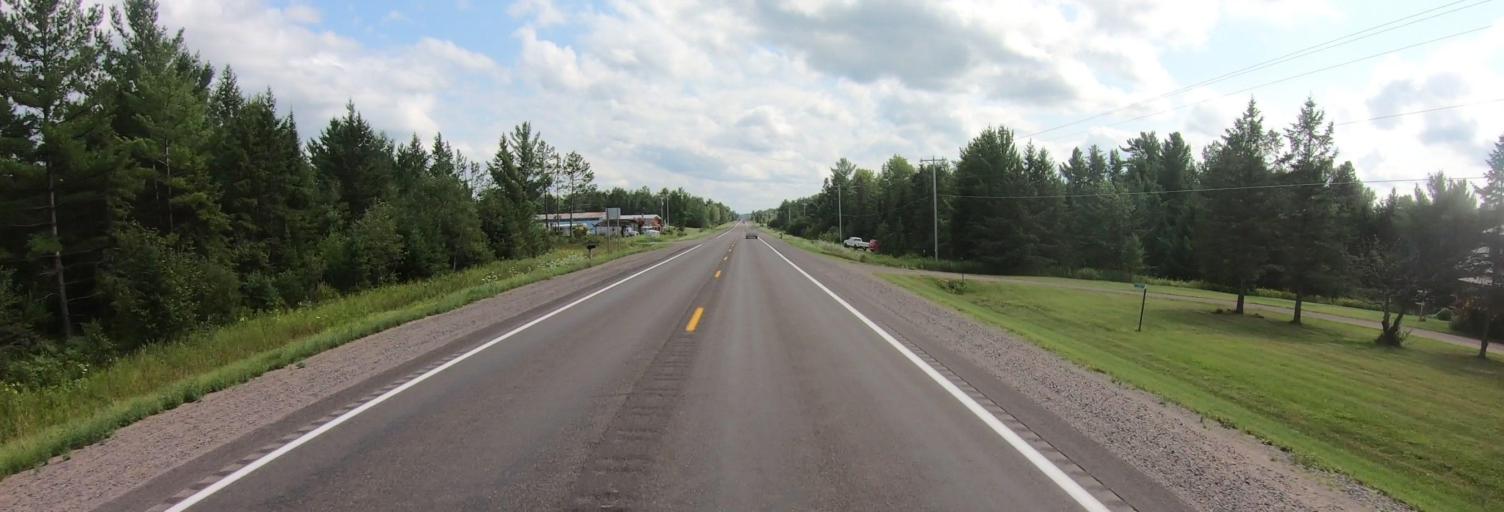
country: US
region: Michigan
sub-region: Ontonagon County
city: Ontonagon
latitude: 46.5506
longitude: -89.1787
